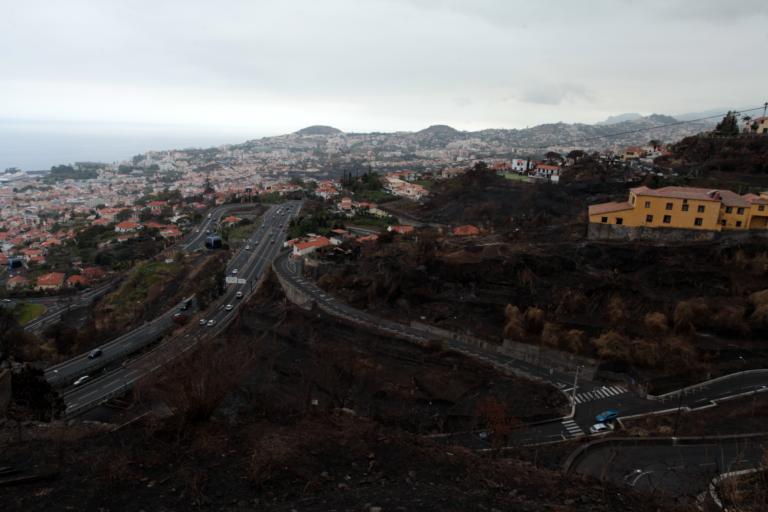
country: PT
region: Madeira
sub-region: Funchal
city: Nossa Senhora do Monte
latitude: 32.6644
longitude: -16.9004
